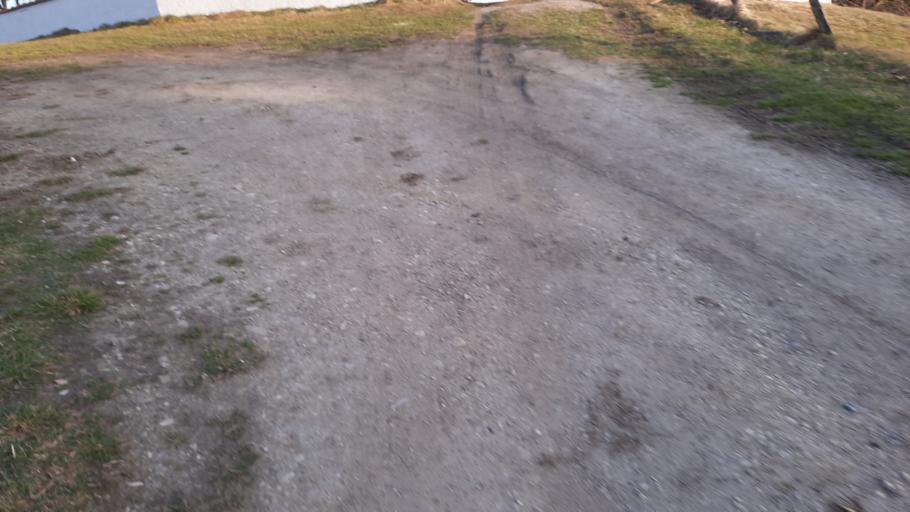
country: DE
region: Bavaria
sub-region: Upper Bavaria
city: Ebersberg
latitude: 48.0792
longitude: 11.9383
